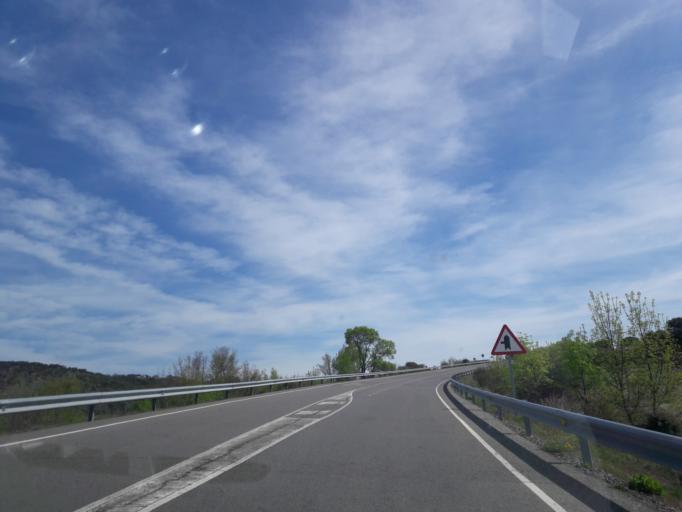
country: ES
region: Castille and Leon
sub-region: Provincia de Salamanca
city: Fuentes de Bejar
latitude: 40.5055
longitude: -5.7002
